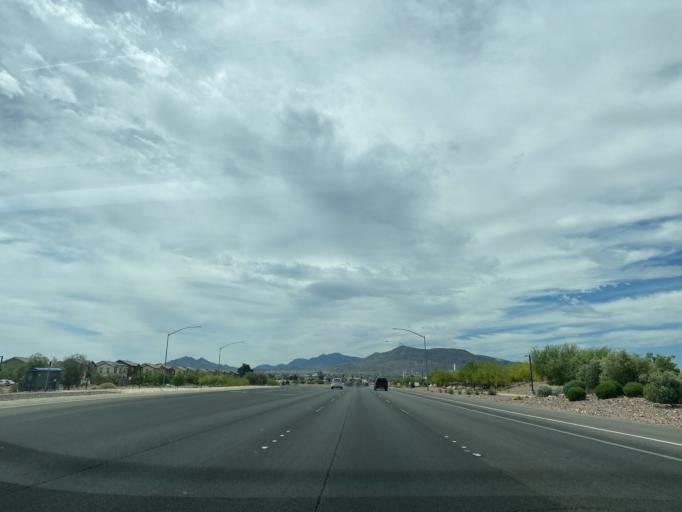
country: US
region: Nevada
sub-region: Clark County
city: Henderson
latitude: 36.0539
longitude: -114.9689
